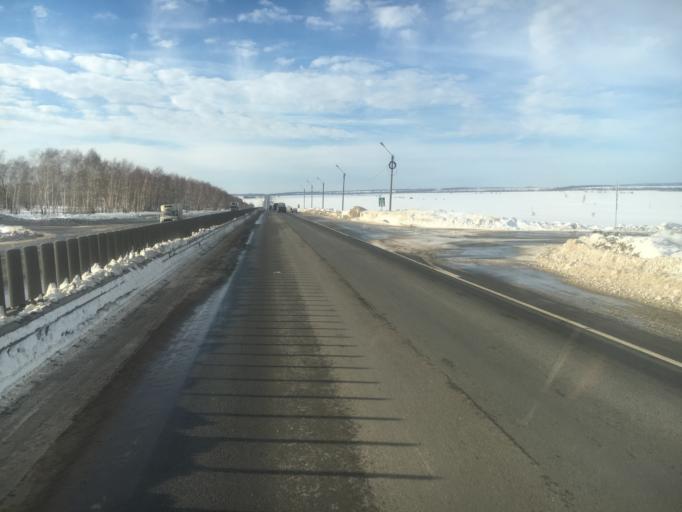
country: RU
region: Samara
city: Mirnyy
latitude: 53.4510
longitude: 50.2448
